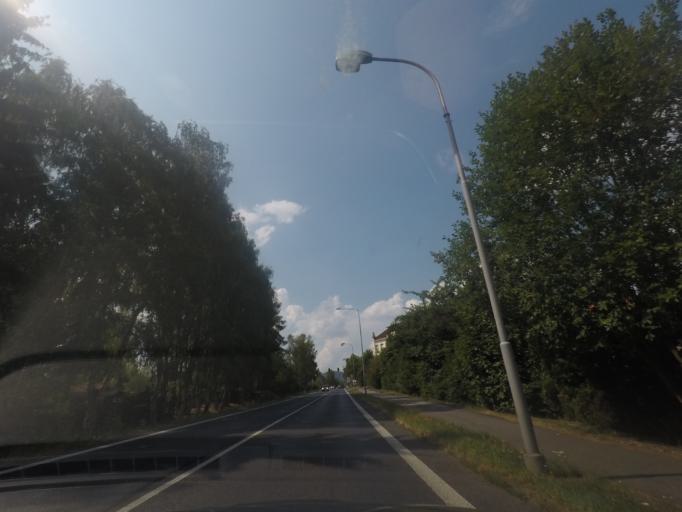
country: CZ
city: Cvikov
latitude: 50.7749
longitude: 14.6302
